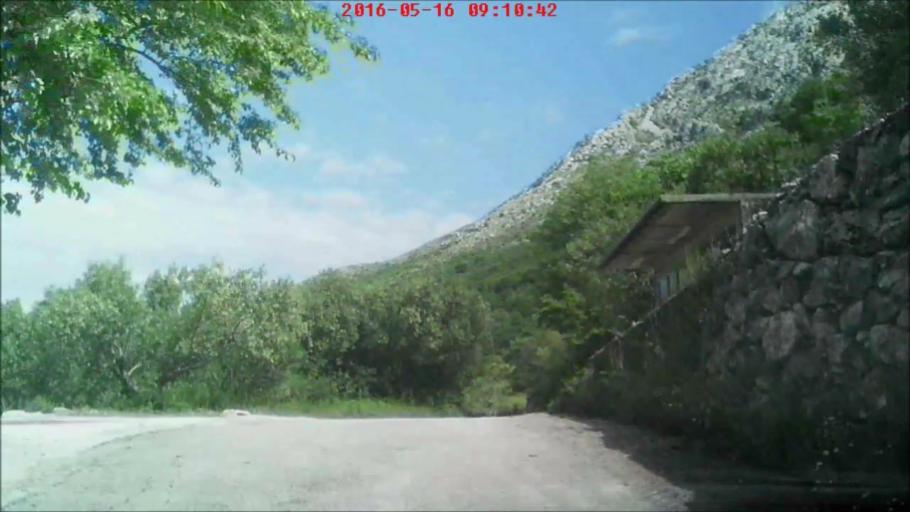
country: HR
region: Dubrovacko-Neretvanska
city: Podgora
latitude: 42.8191
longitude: 17.8559
